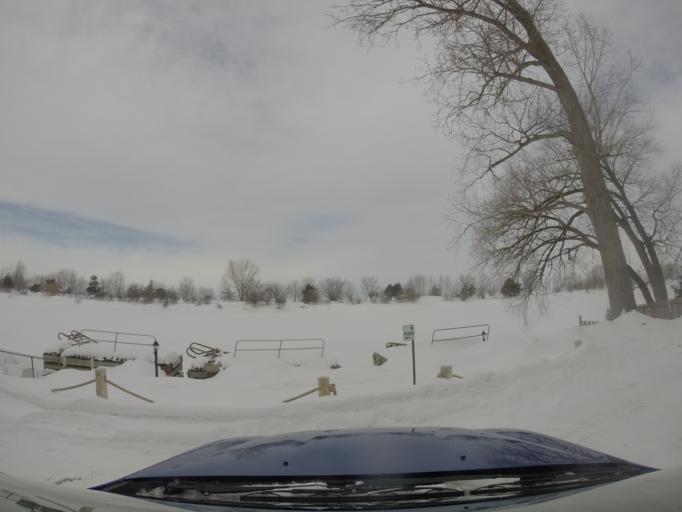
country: CA
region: Ontario
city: Wasaga Beach
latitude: 44.5296
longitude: -80.0112
